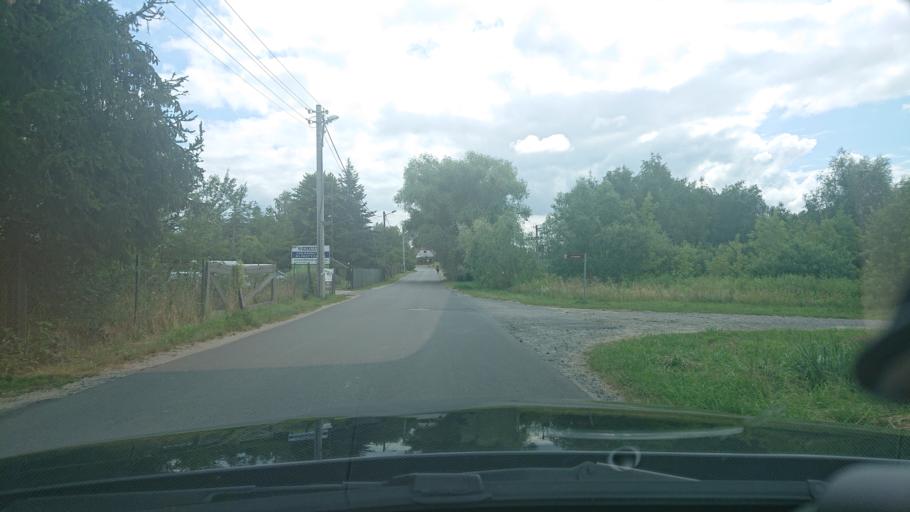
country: PL
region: Greater Poland Voivodeship
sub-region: Powiat gnieznienski
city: Gniezno
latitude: 52.5176
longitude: 17.6203
